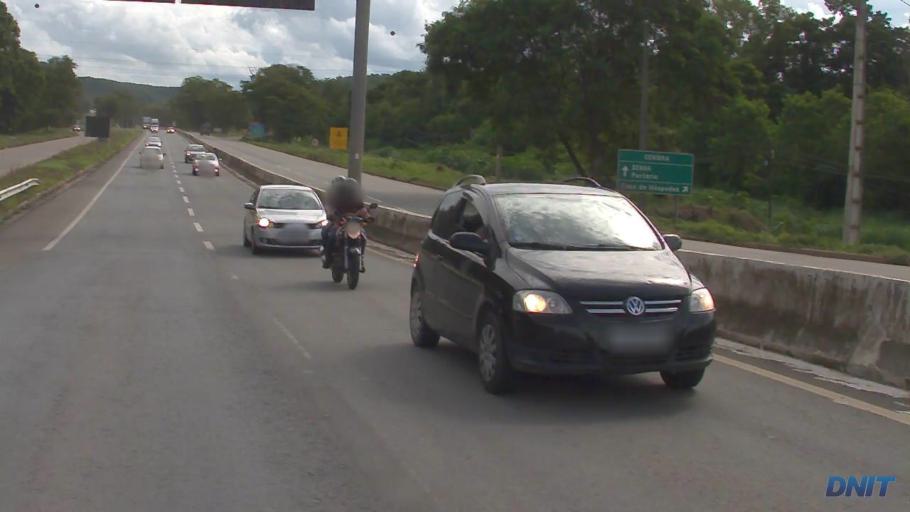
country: BR
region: Minas Gerais
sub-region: Ipaba
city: Ipaba
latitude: -19.3114
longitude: -42.3942
